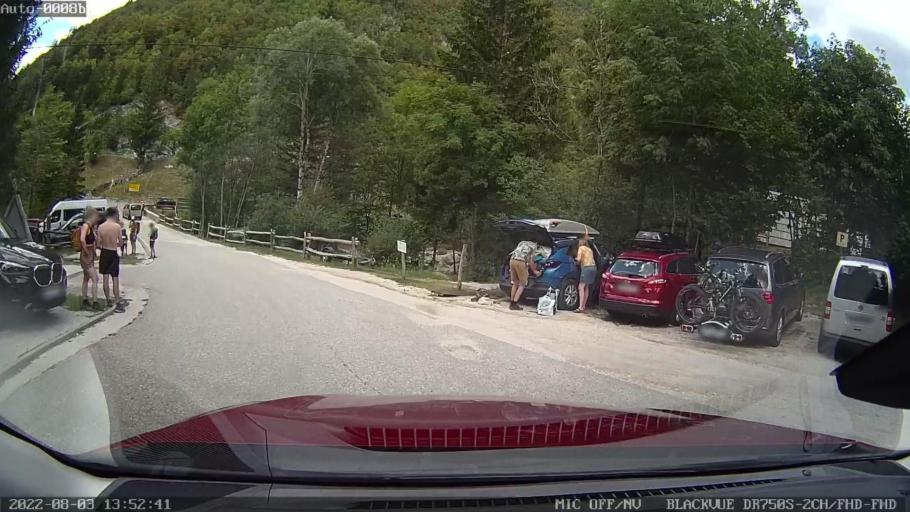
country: SI
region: Bovec
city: Bovec
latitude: 46.3421
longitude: 13.6864
